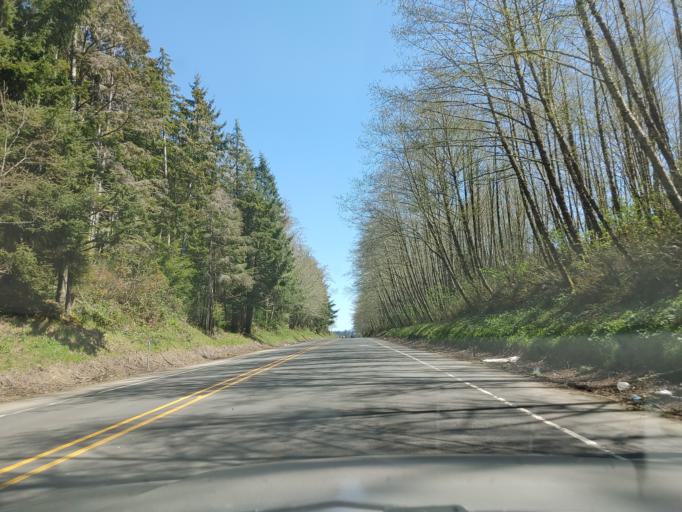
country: US
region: Oregon
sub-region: Clatsop County
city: Warrenton
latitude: 46.1440
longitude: -123.8932
